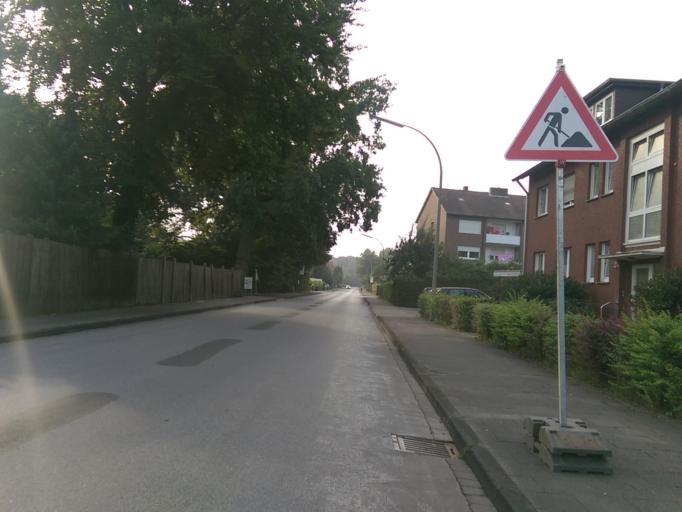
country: DE
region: North Rhine-Westphalia
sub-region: Regierungsbezirk Detmold
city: Harsewinkel
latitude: 51.9549
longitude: 8.2761
